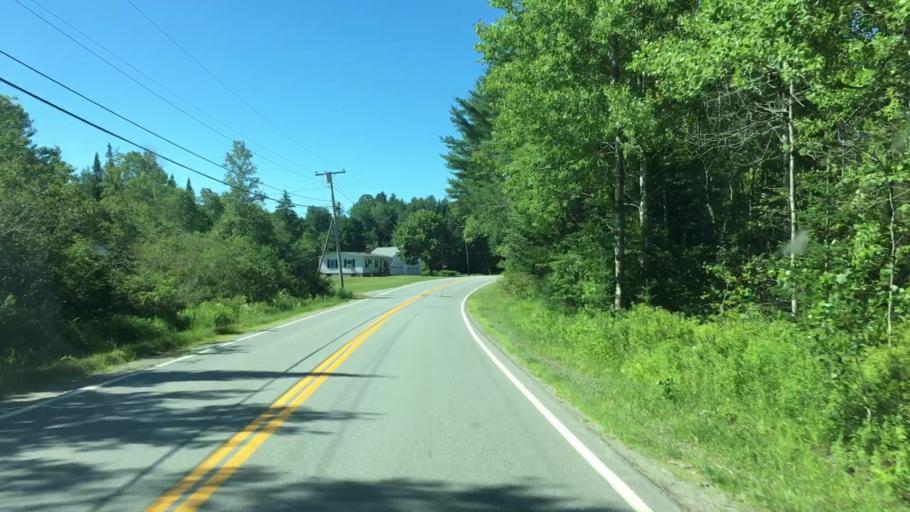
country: US
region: Maine
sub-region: Hancock County
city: Dedham
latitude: 44.7219
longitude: -68.6396
